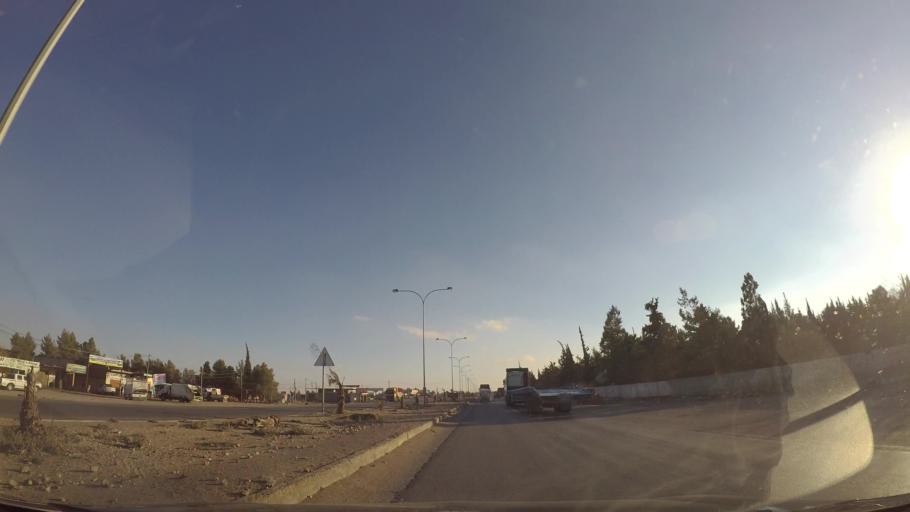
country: JO
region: Tafielah
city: Busayra
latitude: 30.5974
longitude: 35.8042
